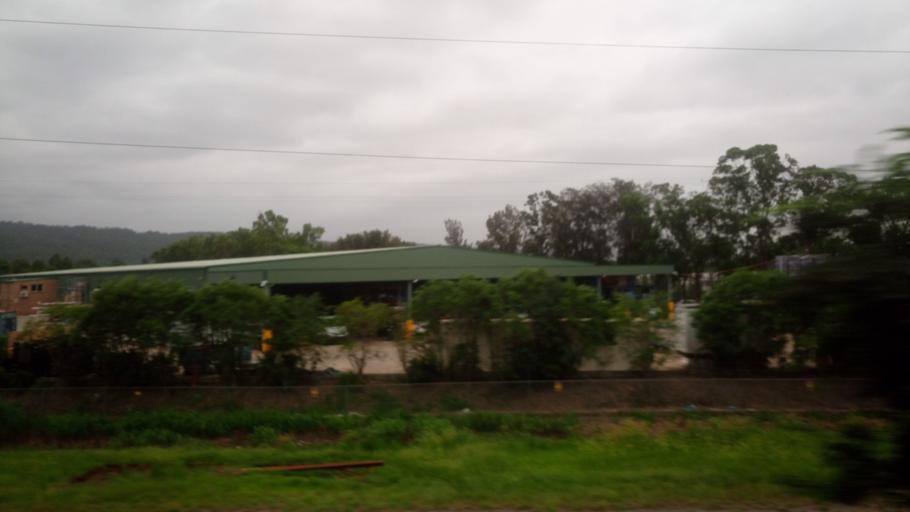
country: AU
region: New South Wales
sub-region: Penrith Municipality
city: Emu Heights
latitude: -33.7471
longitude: 150.6642
